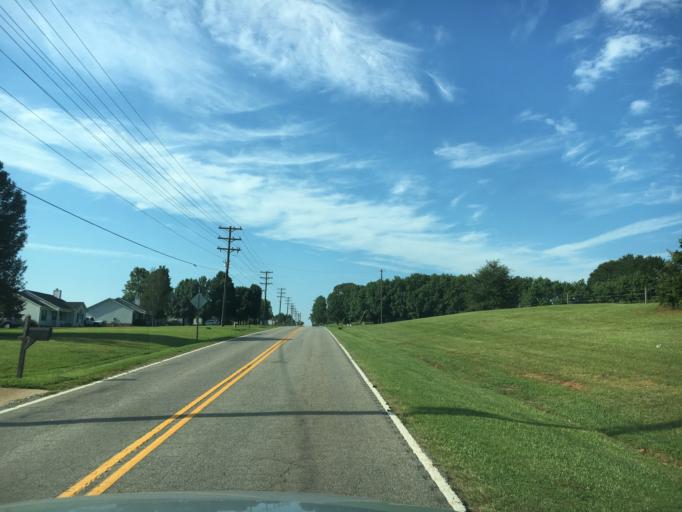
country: US
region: South Carolina
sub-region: Spartanburg County
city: Boiling Springs
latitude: 35.0737
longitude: -81.9291
